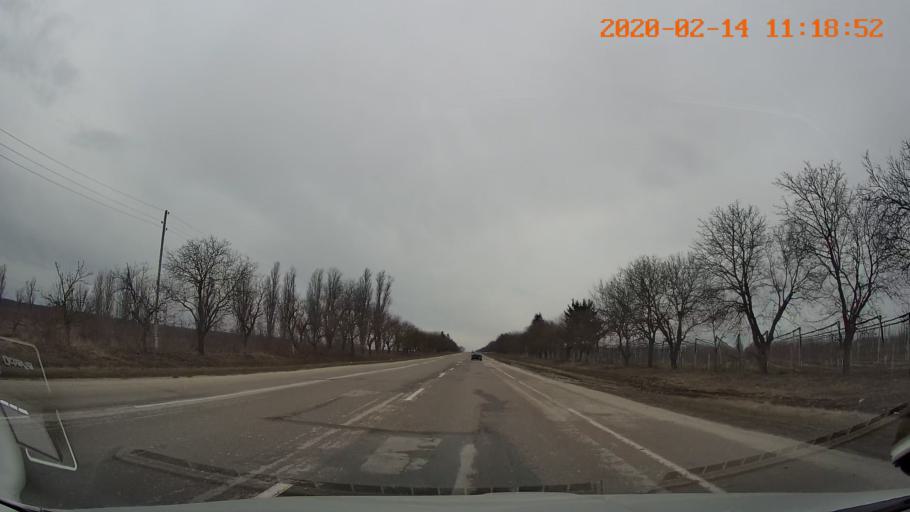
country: MD
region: Briceni
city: Briceni
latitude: 48.2697
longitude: 27.1678
